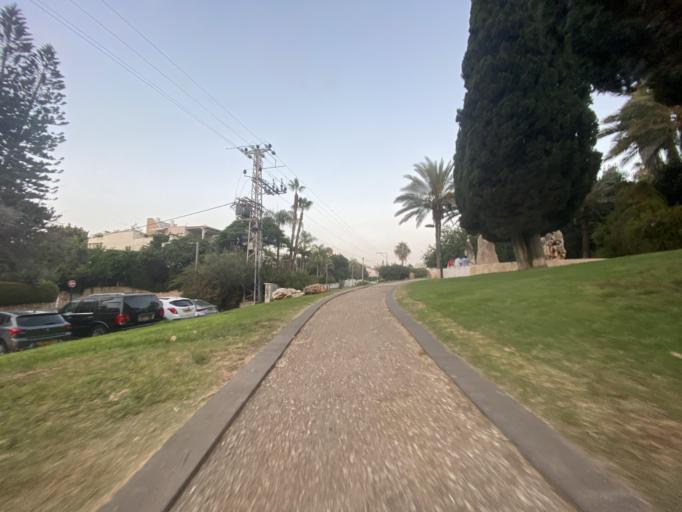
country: IL
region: Tel Aviv
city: Ramat HaSharon
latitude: 32.1468
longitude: 34.8419
